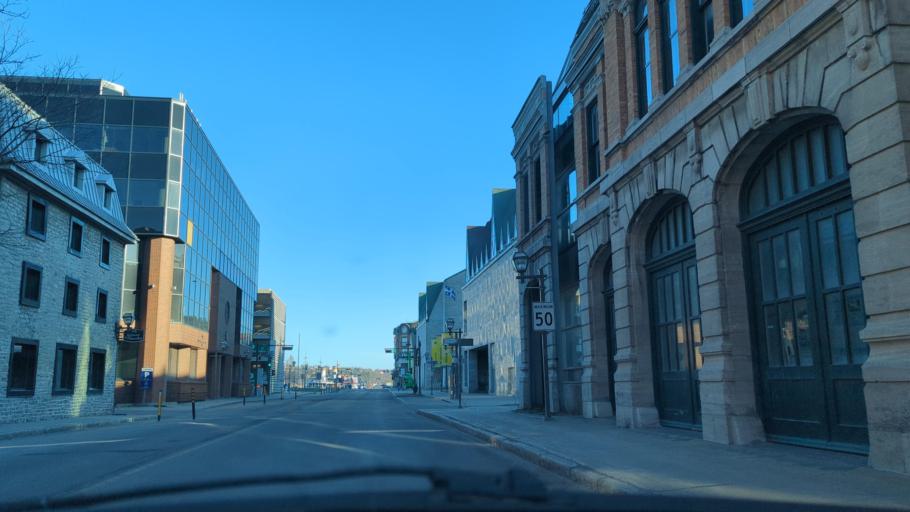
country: CA
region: Quebec
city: Quebec
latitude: 46.8162
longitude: -71.2022
